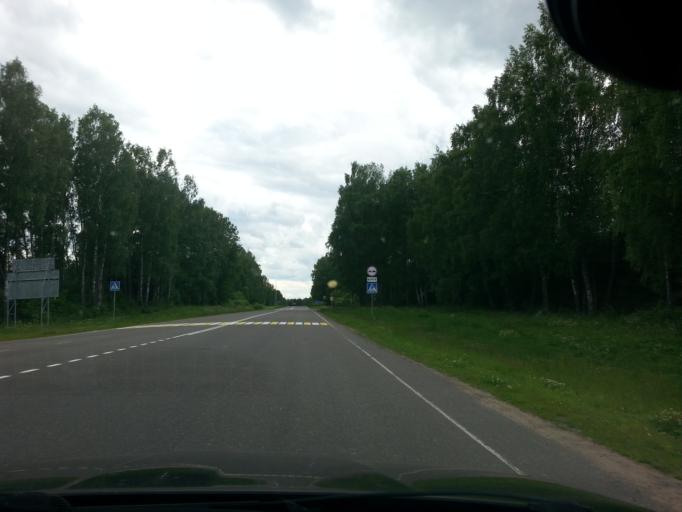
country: BY
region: Minsk
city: Svir
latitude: 54.8917
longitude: 26.3883
